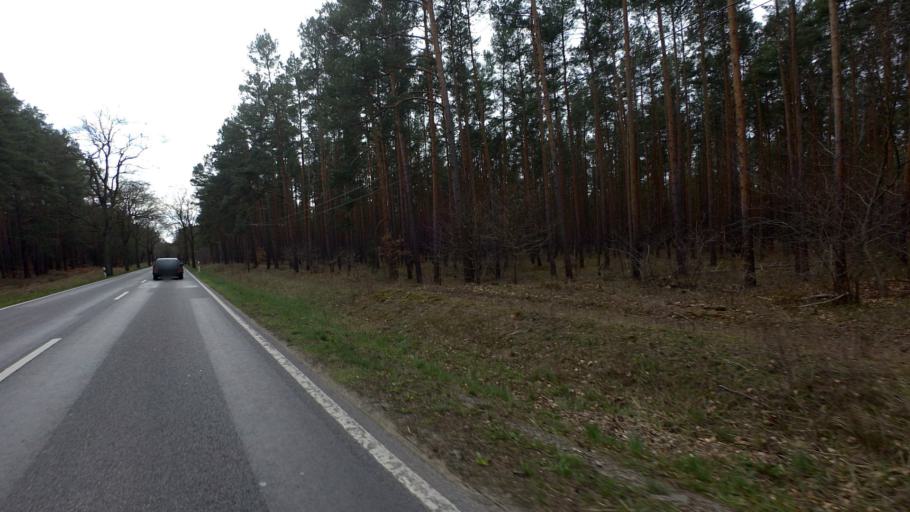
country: DE
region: Brandenburg
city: Glienicke
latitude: 52.7031
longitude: 13.3657
